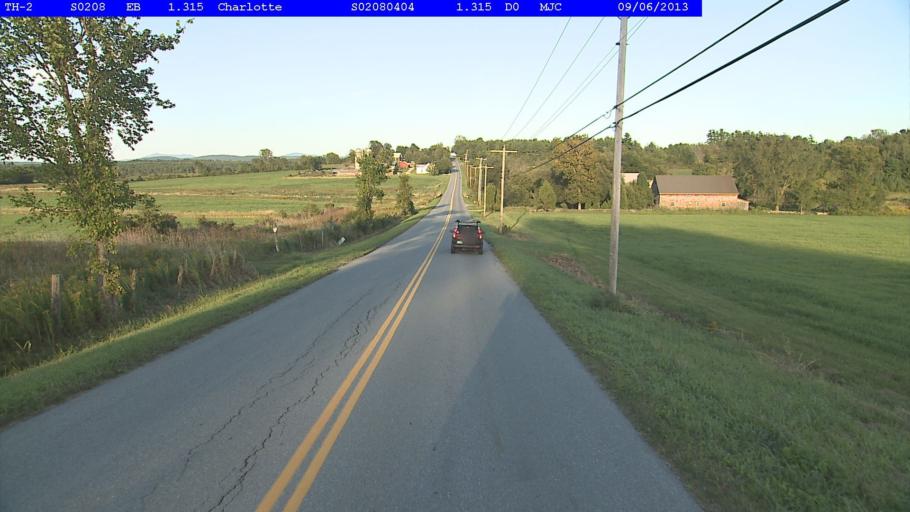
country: US
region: Vermont
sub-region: Chittenden County
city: Hinesburg
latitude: 44.3158
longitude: -73.2221
